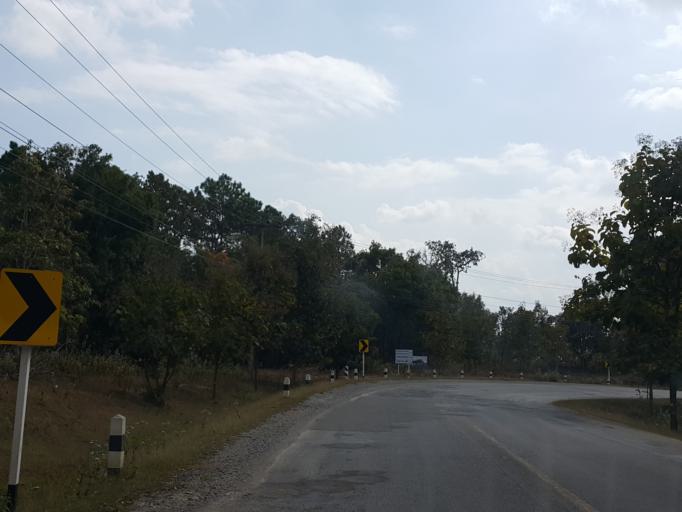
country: TH
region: Chiang Mai
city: Om Koi
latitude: 17.8412
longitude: 98.3740
